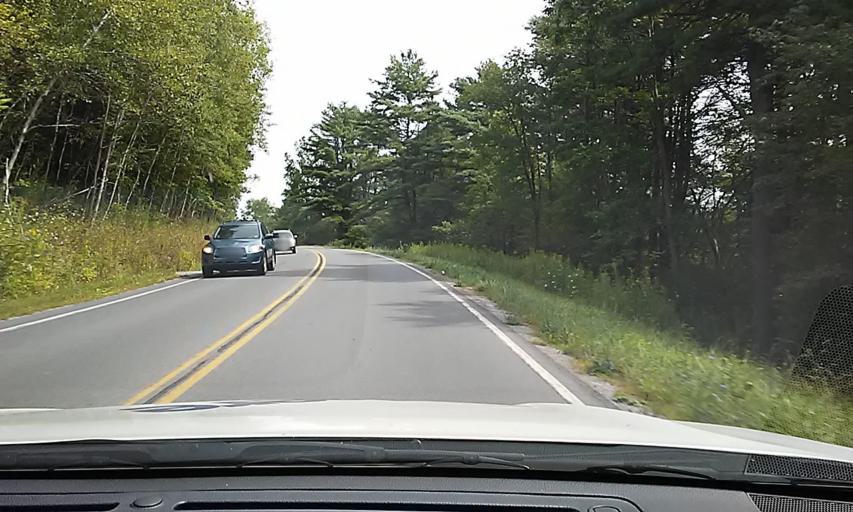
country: US
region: Pennsylvania
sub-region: Elk County
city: Ridgway
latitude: 41.3009
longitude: -78.6658
